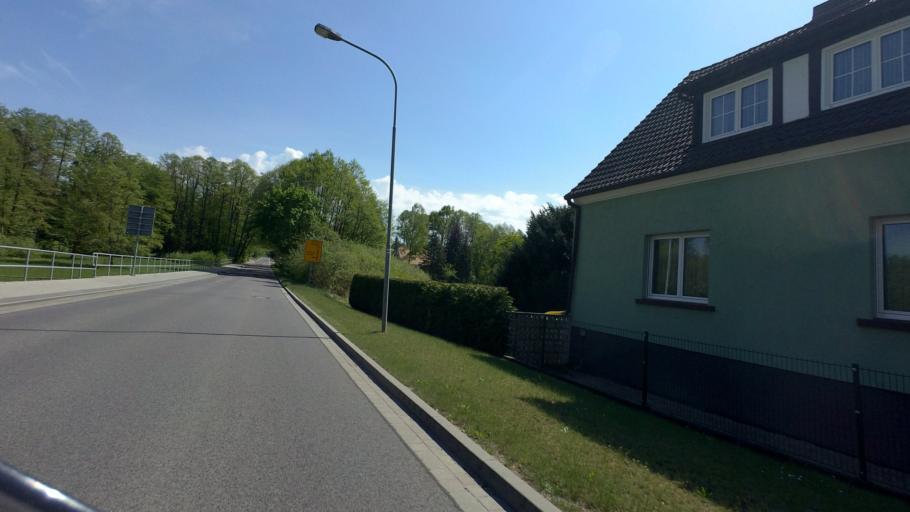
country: DE
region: Brandenburg
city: Neu Zauche
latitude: 52.0107
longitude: 14.1842
